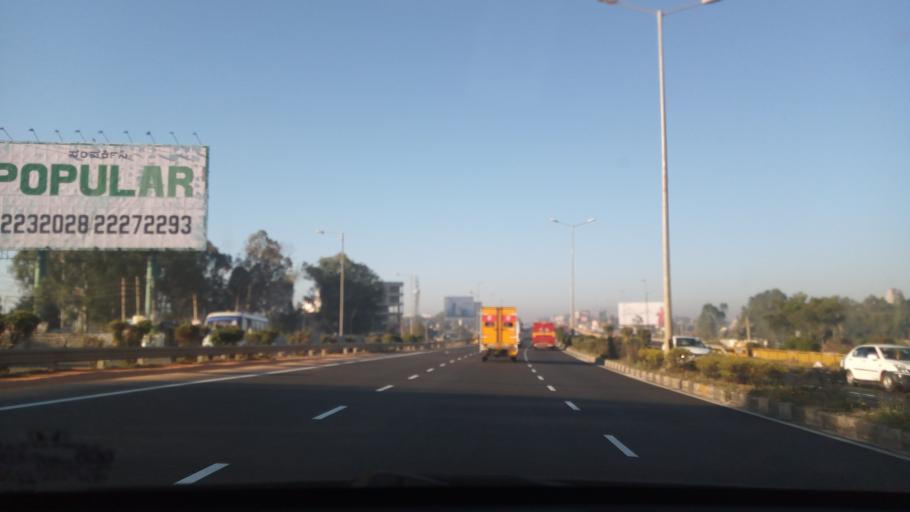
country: IN
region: Karnataka
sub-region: Bangalore Urban
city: Yelahanka
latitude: 13.1653
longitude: 77.6301
